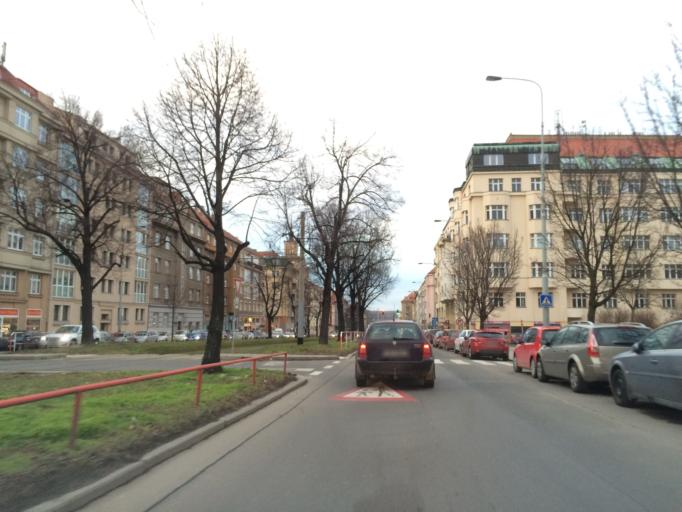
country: CZ
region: Praha
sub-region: Praha 1
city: Mala Strana
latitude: 50.1057
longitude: 14.3949
